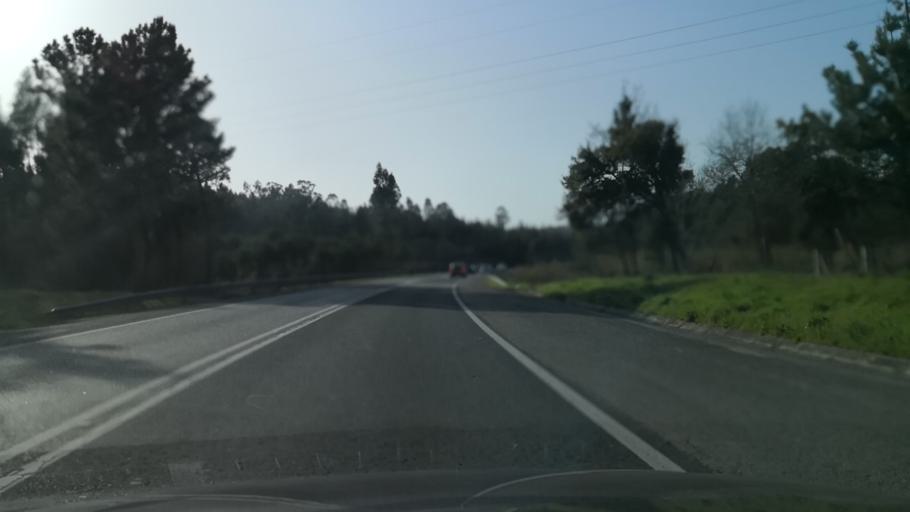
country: PT
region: Leiria
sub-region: Leiria
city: Leiria
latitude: 39.7431
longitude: -8.8414
